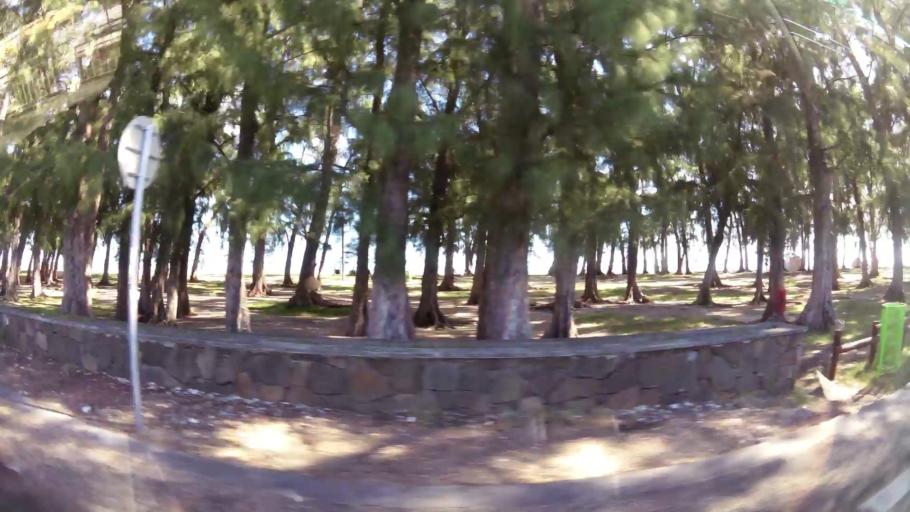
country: MU
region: Black River
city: Flic en Flac
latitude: -20.2824
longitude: 57.3652
